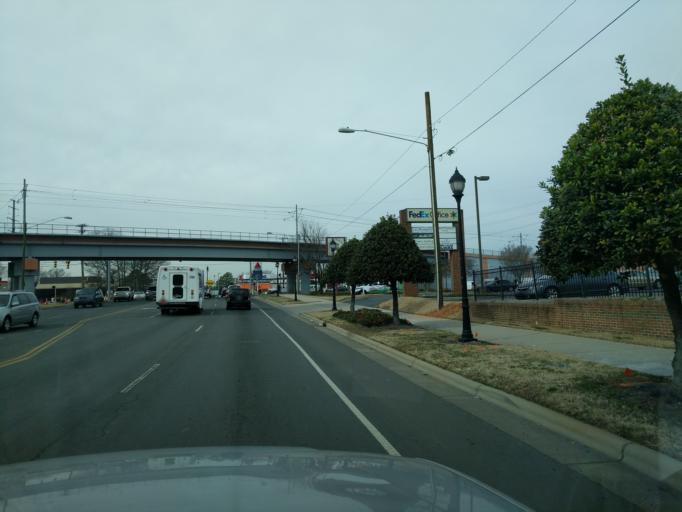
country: US
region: North Carolina
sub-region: Mecklenburg County
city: Charlotte
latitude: 35.1776
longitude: -80.8783
